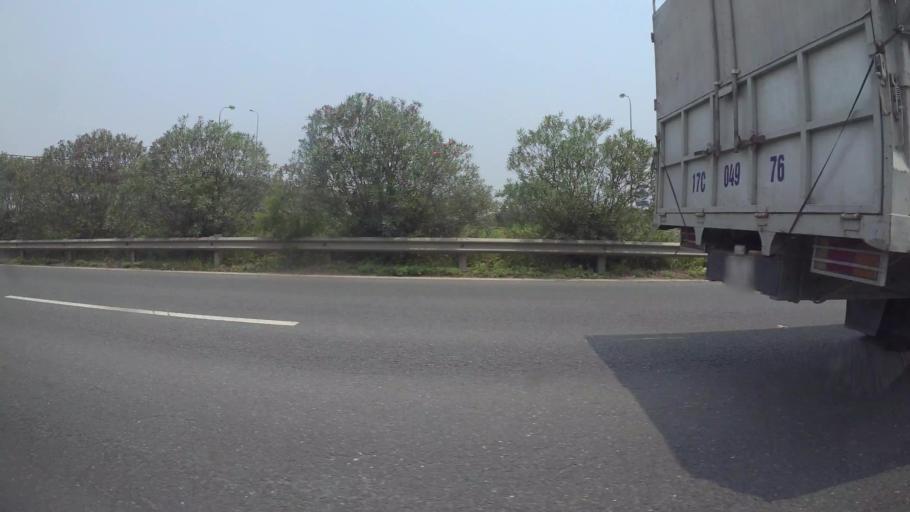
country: VN
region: Ha Noi
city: Quoc Oai
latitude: 21.0030
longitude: 105.6503
